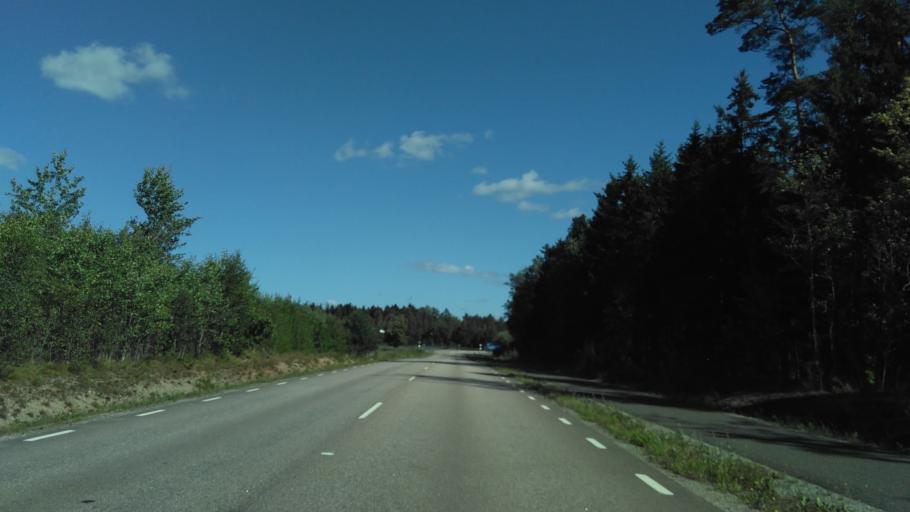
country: SE
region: Vaestra Goetaland
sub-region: Skara Kommun
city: Axvall
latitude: 58.4001
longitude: 13.5472
